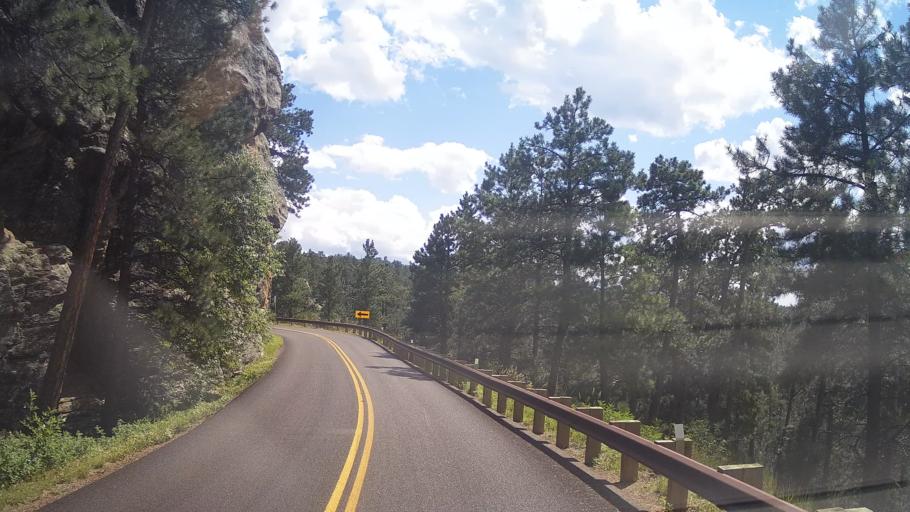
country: US
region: South Dakota
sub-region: Custer County
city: Custer
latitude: 43.8617
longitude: -103.4414
